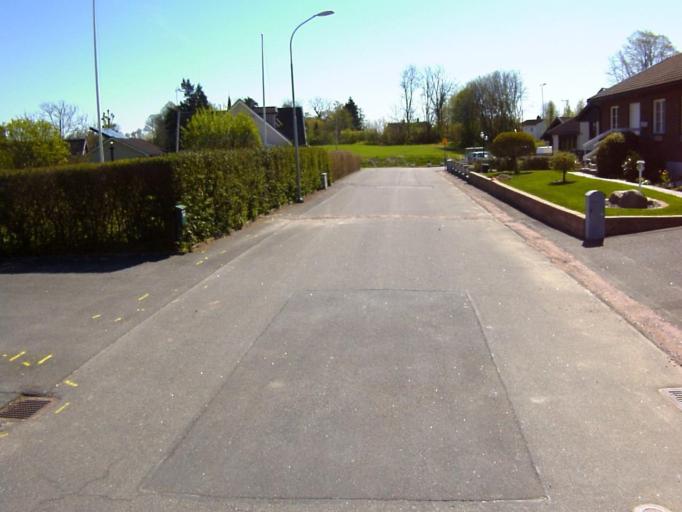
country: SE
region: Skane
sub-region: Kristianstads Kommun
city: Kristianstad
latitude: 56.0532
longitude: 14.1880
